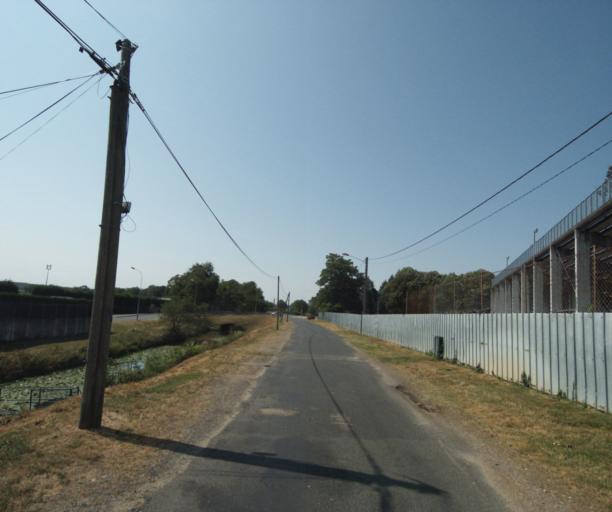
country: FR
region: Bourgogne
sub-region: Departement de Saone-et-Loire
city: Gueugnon
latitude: 46.5949
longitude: 4.0574
